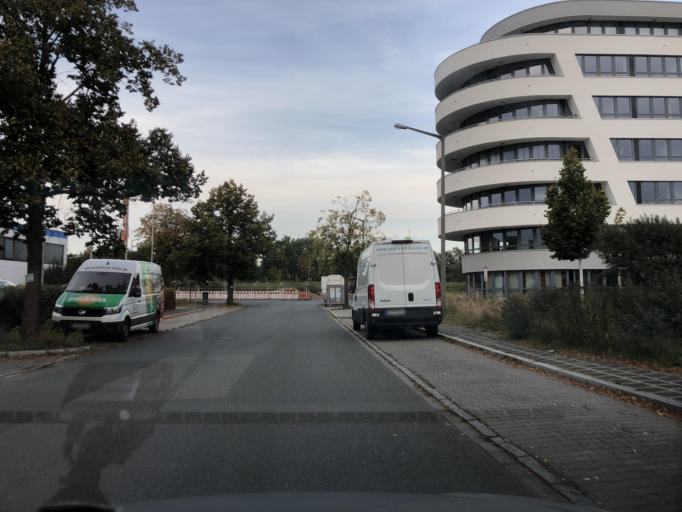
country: DE
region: Bavaria
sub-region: Regierungsbezirk Mittelfranken
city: Grossreuth bei Schweinau
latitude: 49.4369
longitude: 11.0015
